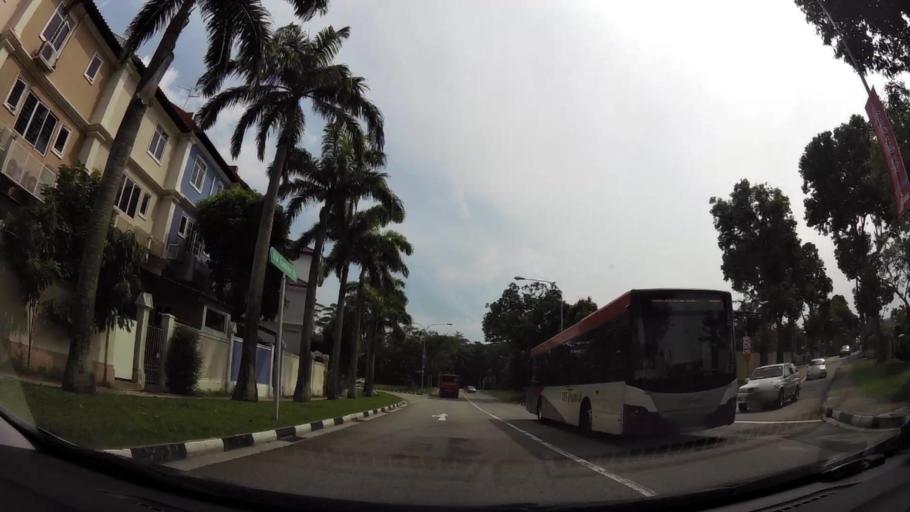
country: SG
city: Singapore
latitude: 1.3633
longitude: 103.9678
